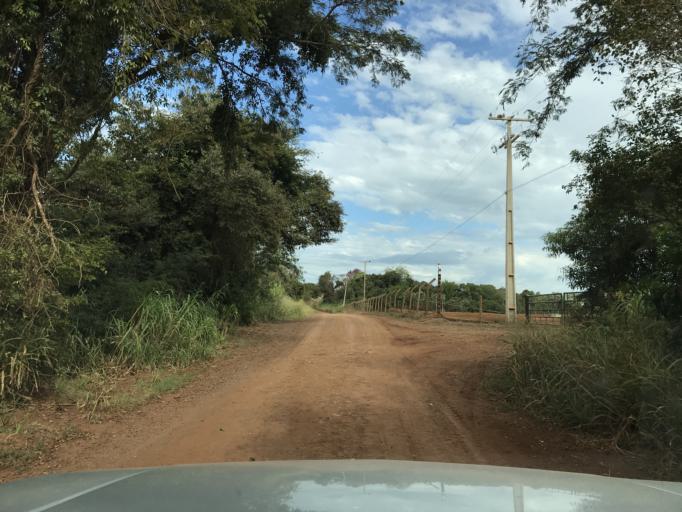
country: BR
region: Parana
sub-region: Palotina
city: Palotina
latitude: -24.3225
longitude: -53.8060
